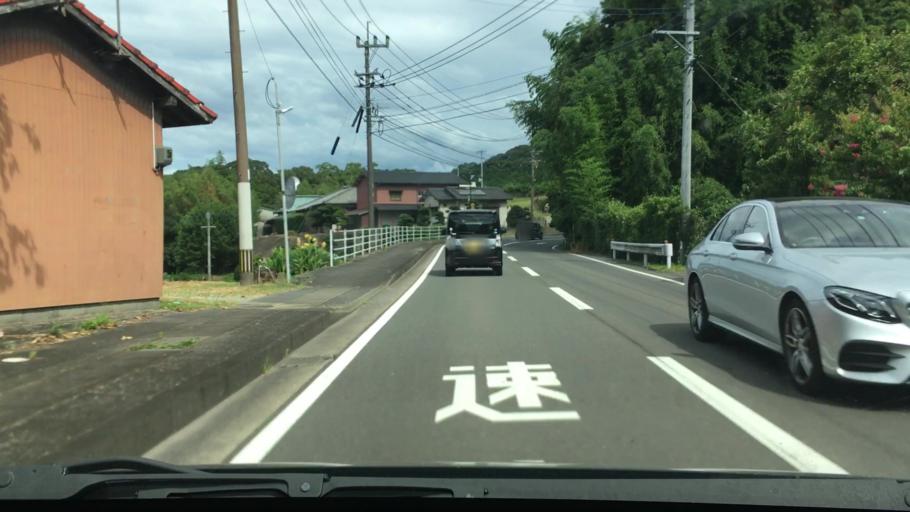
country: JP
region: Nagasaki
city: Togitsu
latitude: 32.9169
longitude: 129.7863
